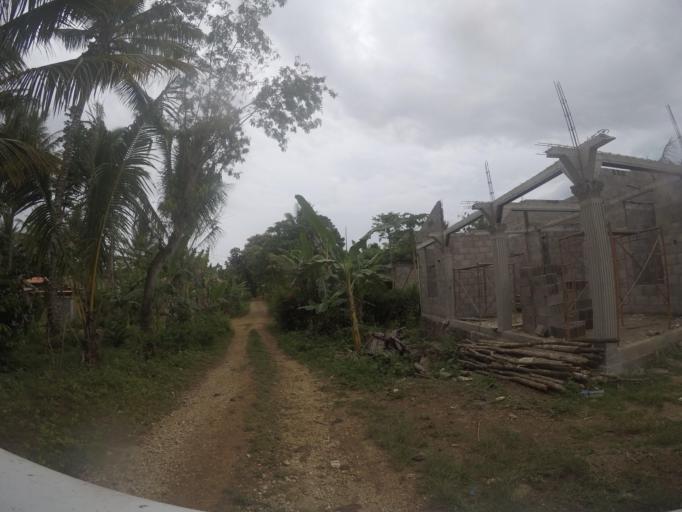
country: TL
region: Lautem
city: Lospalos
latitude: -8.5295
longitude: 126.9934
